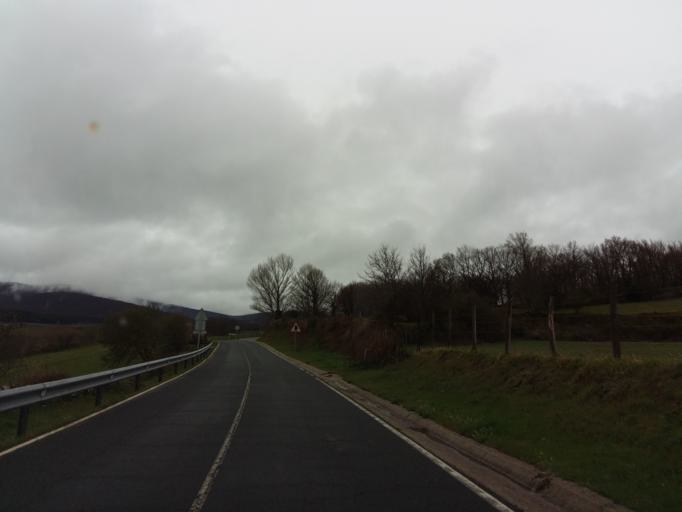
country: ES
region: Cantabria
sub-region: Provincia de Cantabria
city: Villaescusa
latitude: 42.9354
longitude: -4.2023
